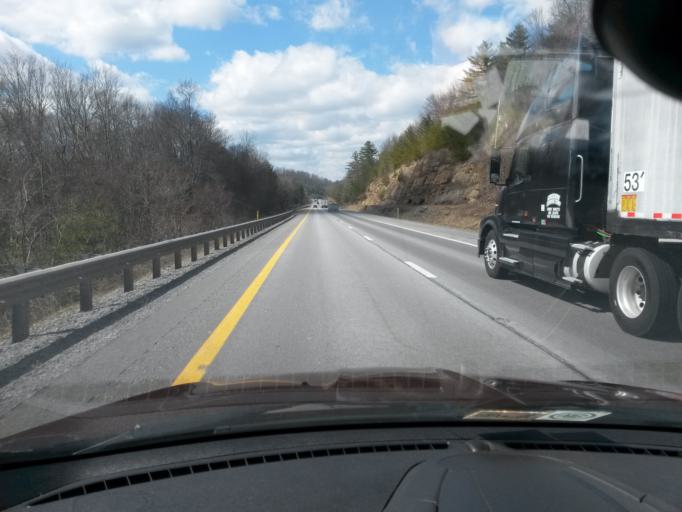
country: US
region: West Virginia
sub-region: Raleigh County
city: Shady Spring
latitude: 37.7000
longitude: -81.1392
